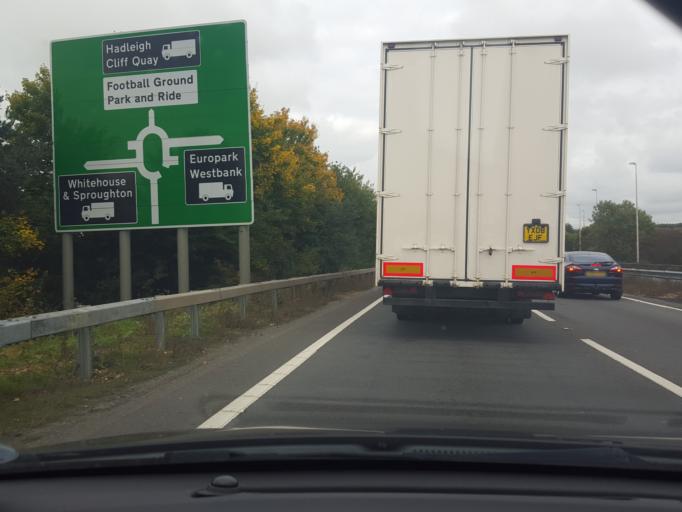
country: GB
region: England
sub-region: Suffolk
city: Bramford
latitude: 52.0336
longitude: 1.0962
